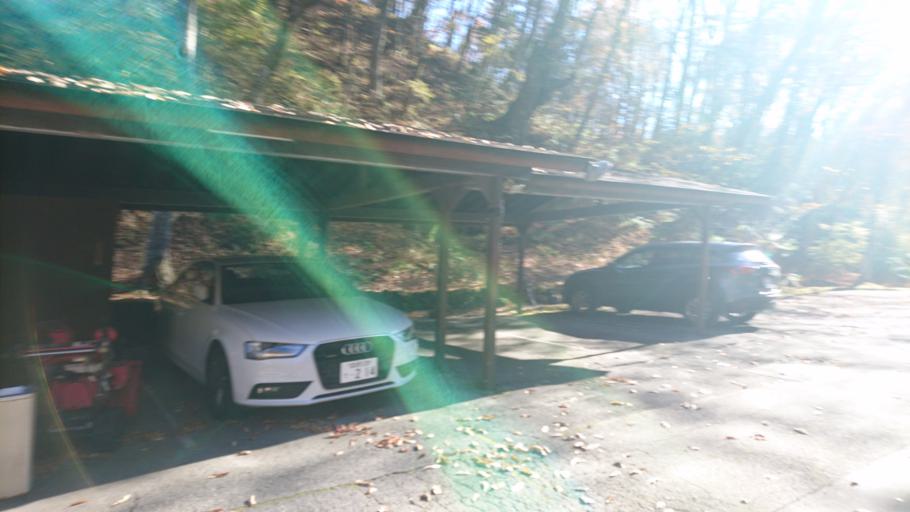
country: JP
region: Nagano
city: Komoro
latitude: 36.3893
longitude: 138.6145
